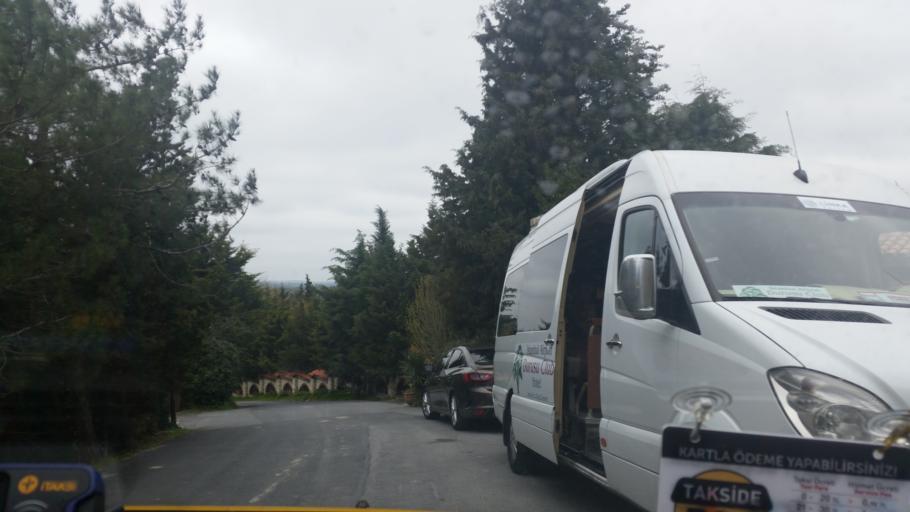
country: TR
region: Istanbul
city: Boyalik
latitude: 41.2882
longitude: 28.6037
